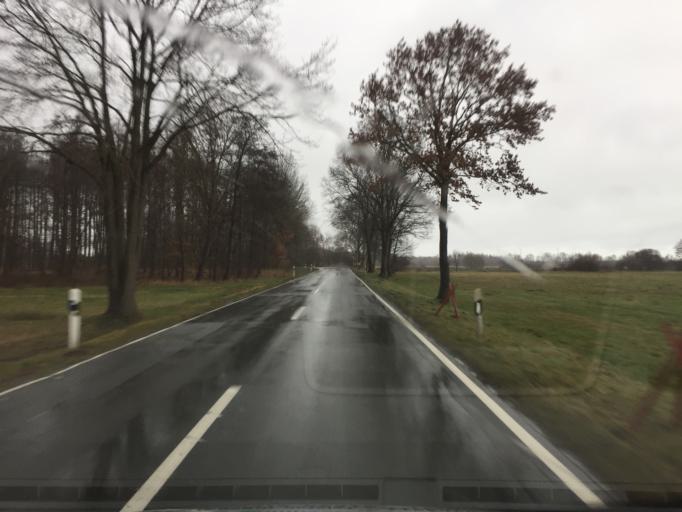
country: DE
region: Lower Saxony
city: Maasen
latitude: 52.6359
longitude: 8.8900
